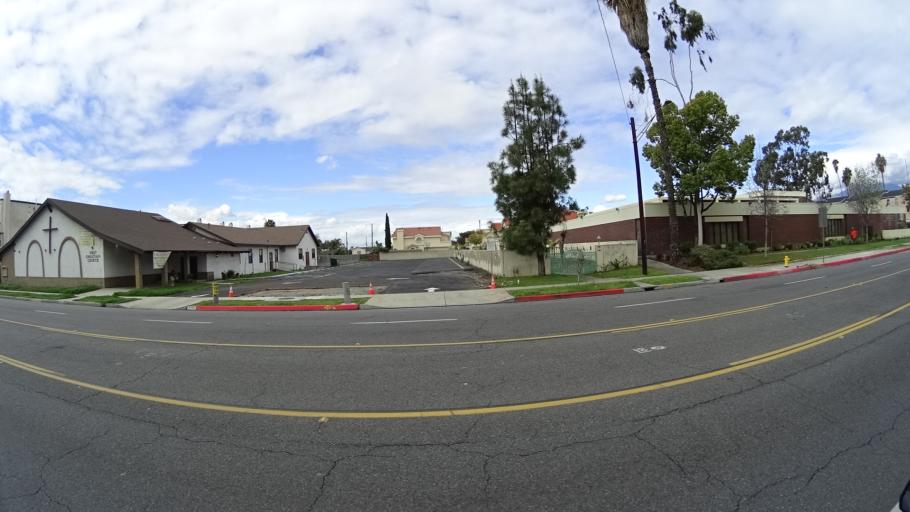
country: US
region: California
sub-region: Los Angeles County
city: Baldwin Park
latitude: 34.0878
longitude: -117.9647
